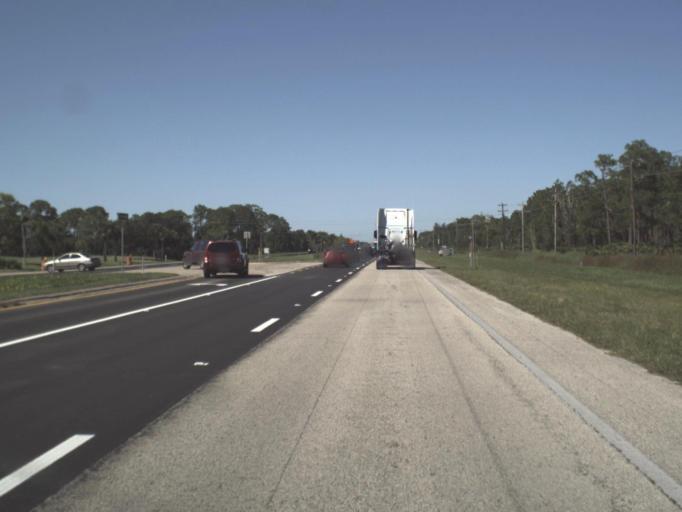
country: US
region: Florida
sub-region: Lee County
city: Suncoast Estates
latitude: 26.7522
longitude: -81.9213
